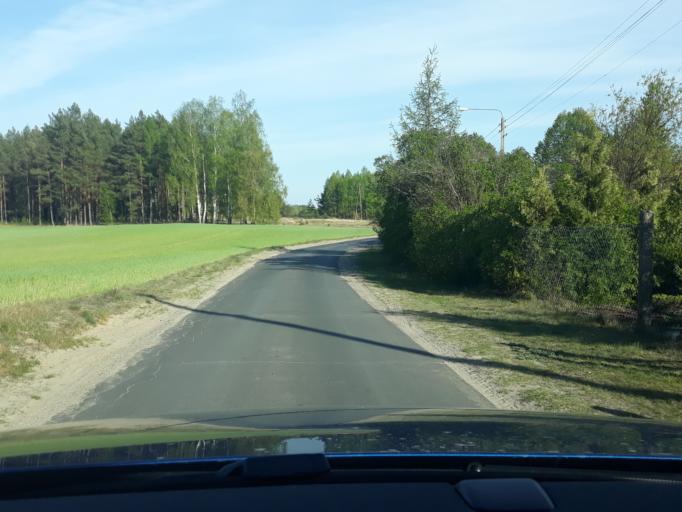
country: PL
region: Pomeranian Voivodeship
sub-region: Powiat czluchowski
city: Przechlewo
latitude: 53.8814
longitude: 17.3216
